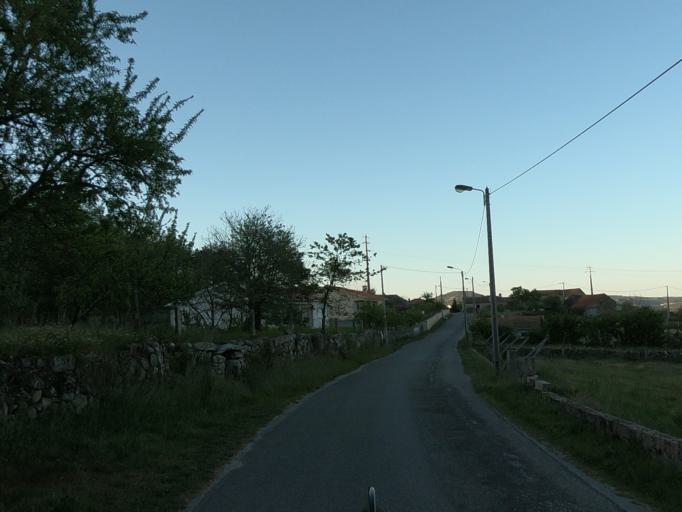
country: PT
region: Vila Real
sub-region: Sabrosa
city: Sabrosa
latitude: 41.3440
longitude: -7.6225
